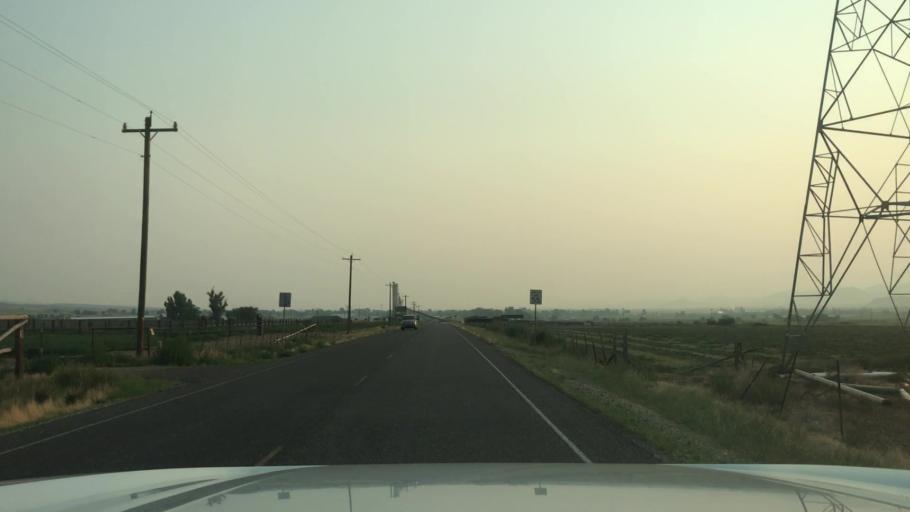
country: US
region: Utah
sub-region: Sevier County
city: Aurora
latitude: 38.8982
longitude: -111.9492
